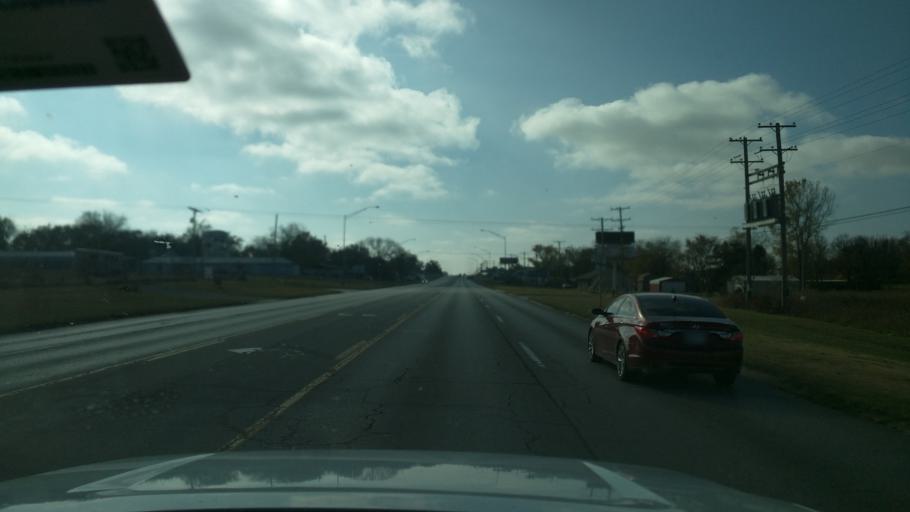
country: US
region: Oklahoma
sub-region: Washington County
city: Dewey
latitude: 36.7724
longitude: -95.9355
